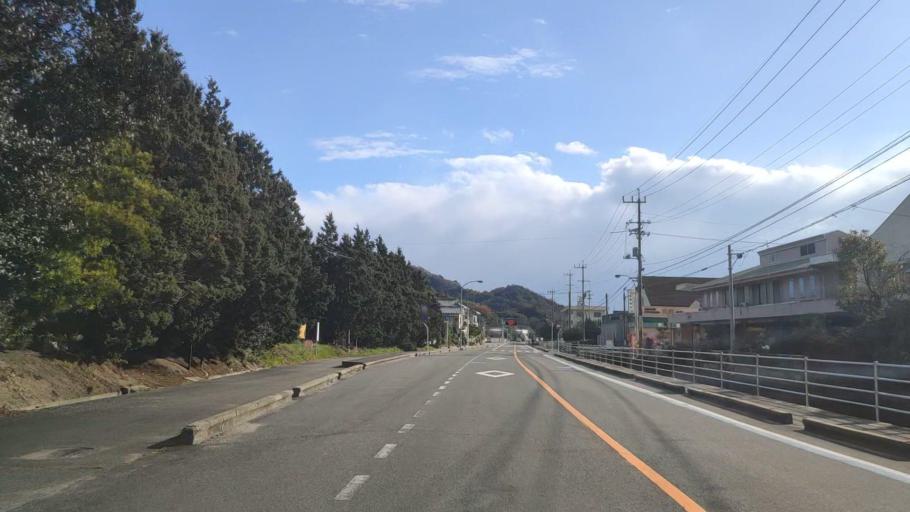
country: JP
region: Hiroshima
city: Innoshima
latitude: 34.2080
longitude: 133.0736
